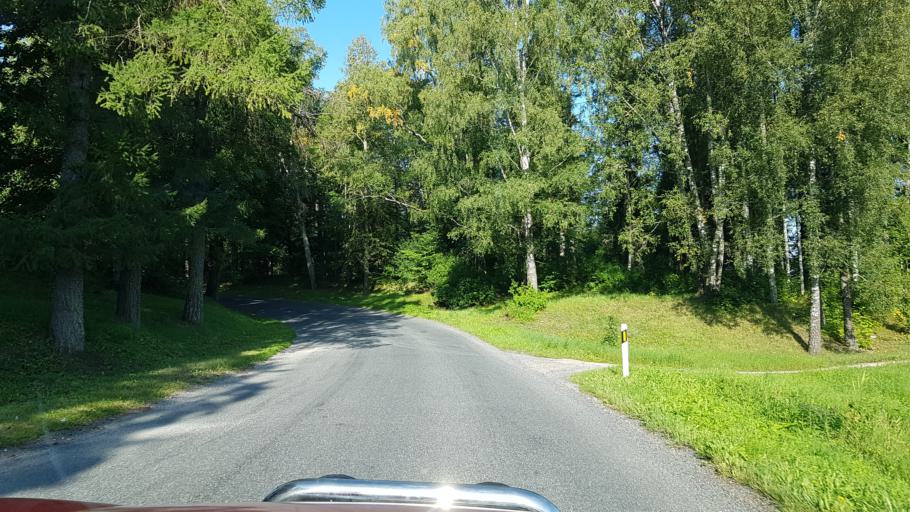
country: EE
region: Vorumaa
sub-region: Antsla vald
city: Vana-Antsla
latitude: 57.7433
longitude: 26.6548
